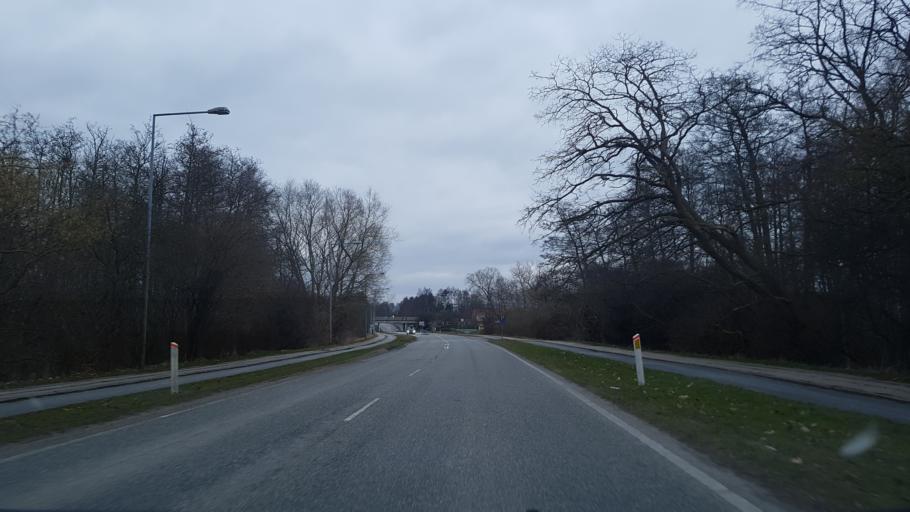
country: DK
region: Zealand
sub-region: Soro Kommune
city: Frederiksberg
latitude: 55.4215
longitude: 11.5648
